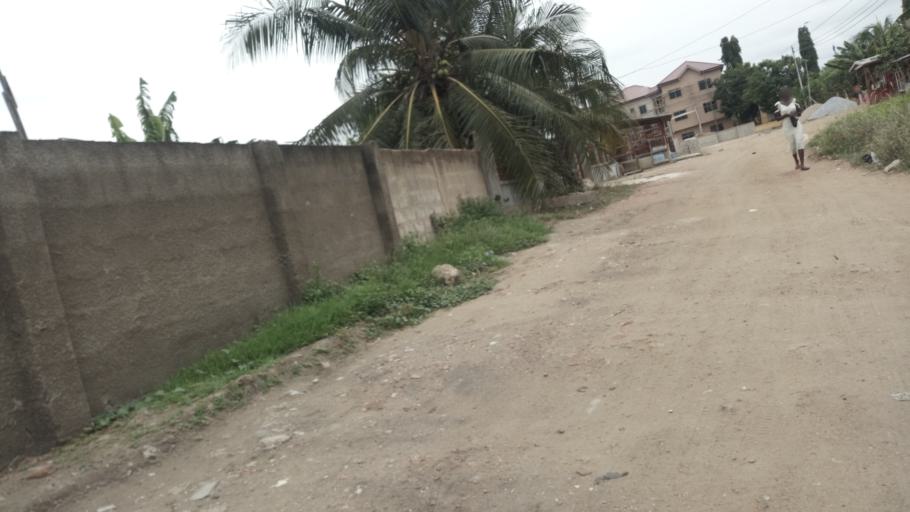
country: GH
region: Central
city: Winneba
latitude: 5.3679
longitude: -0.6395
